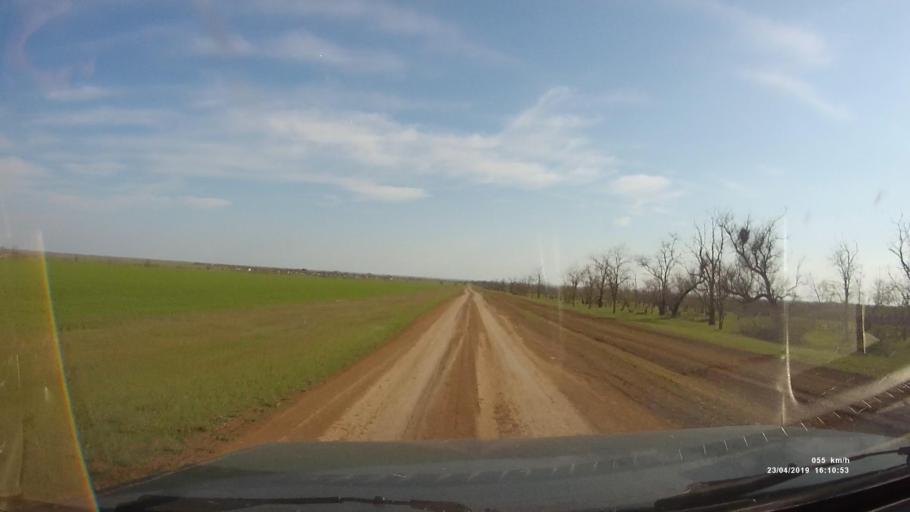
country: RU
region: Rostov
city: Remontnoye
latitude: 46.4787
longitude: 43.1231
